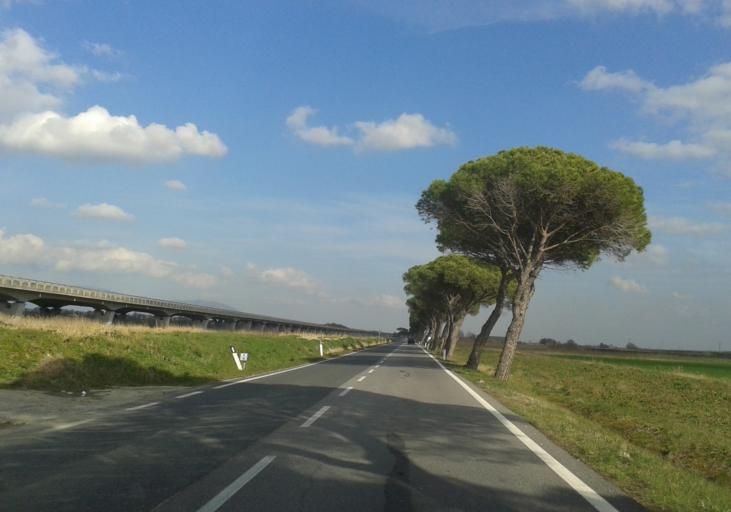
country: IT
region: Tuscany
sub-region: Provincia di Livorno
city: Guasticce
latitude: 43.6127
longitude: 10.3882
